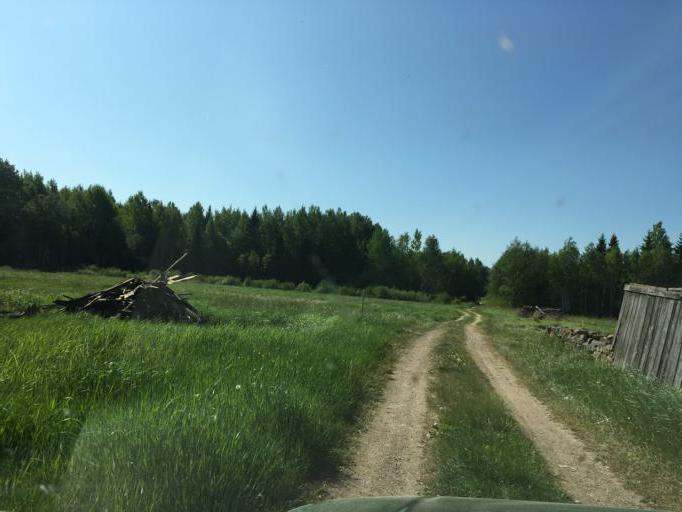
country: LV
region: Ventspils
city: Ventspils
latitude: 57.4806
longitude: 21.7630
